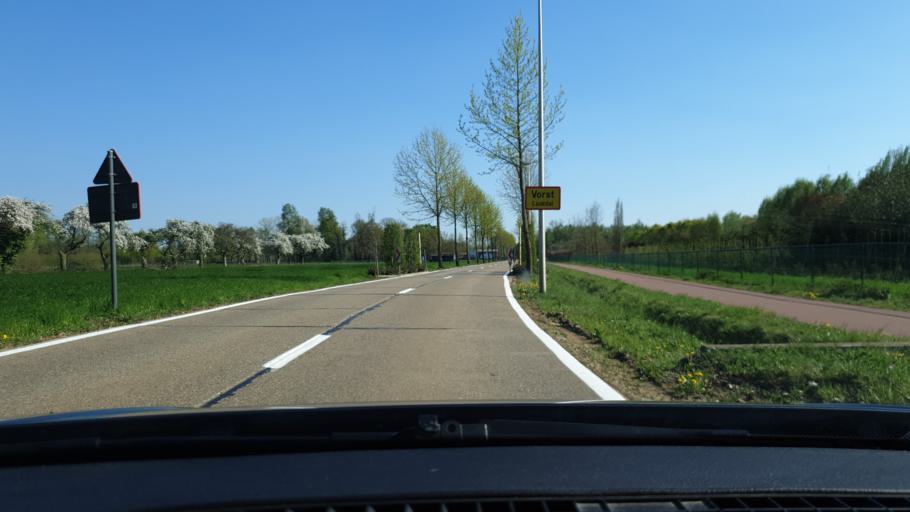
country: BE
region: Flanders
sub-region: Provincie Antwerpen
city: Laakdal
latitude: 51.0924
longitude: 5.0156
